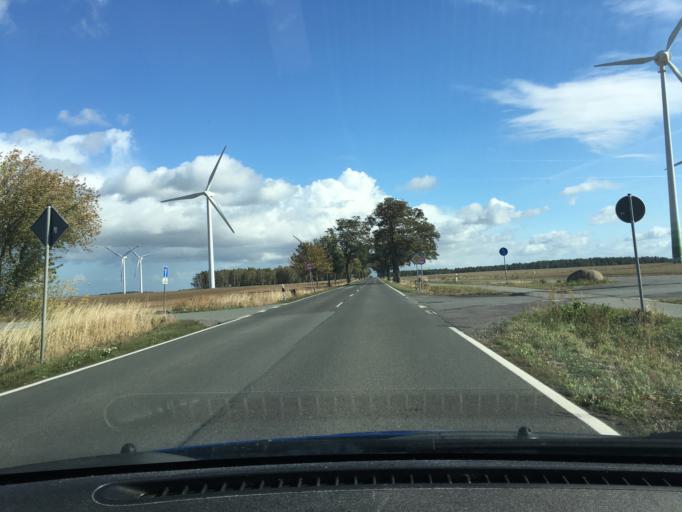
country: DE
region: Saxony-Anhalt
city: Pretzier
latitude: 52.8391
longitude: 11.2218
